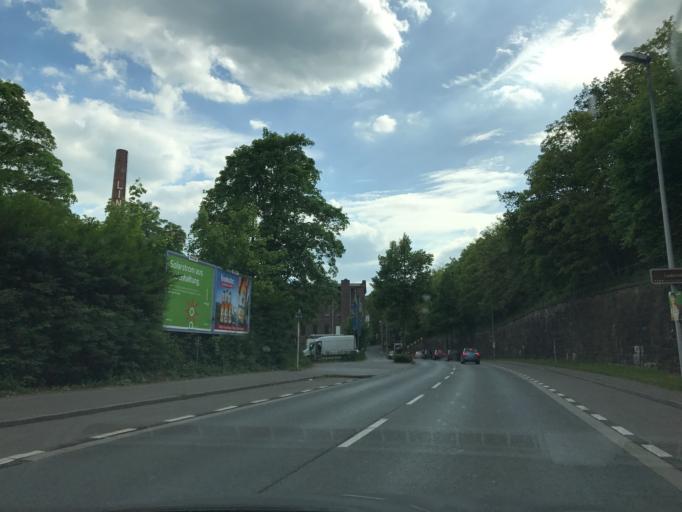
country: DE
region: North Rhine-Westphalia
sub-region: Regierungsbezirk Dusseldorf
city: Muelheim (Ruhr)
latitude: 51.4179
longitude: 6.8692
